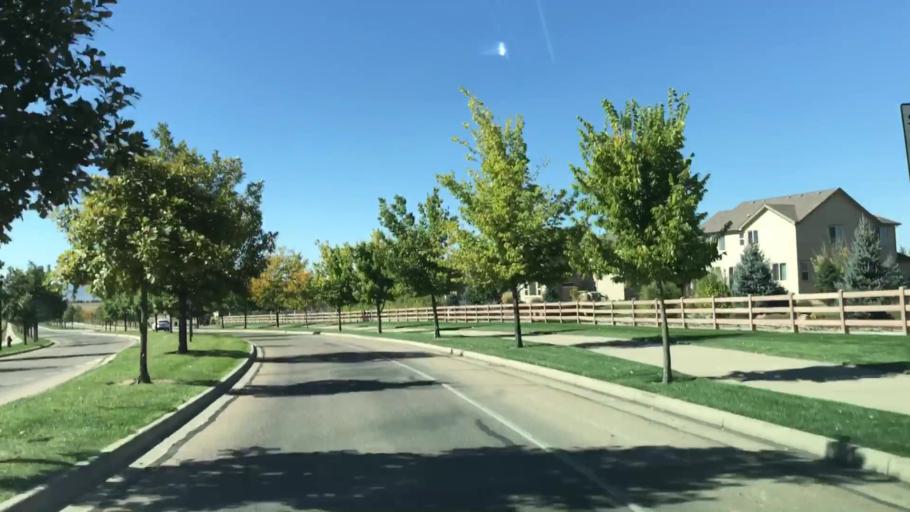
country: US
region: Colorado
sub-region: Weld County
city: Windsor
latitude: 40.4421
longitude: -104.9683
